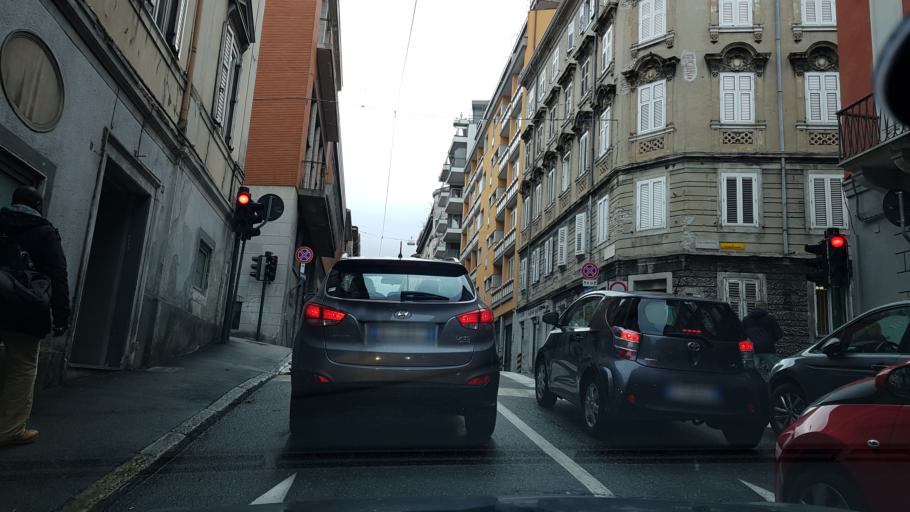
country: IT
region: Friuli Venezia Giulia
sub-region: Provincia di Trieste
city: Trieste
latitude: 45.6516
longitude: 13.7839
